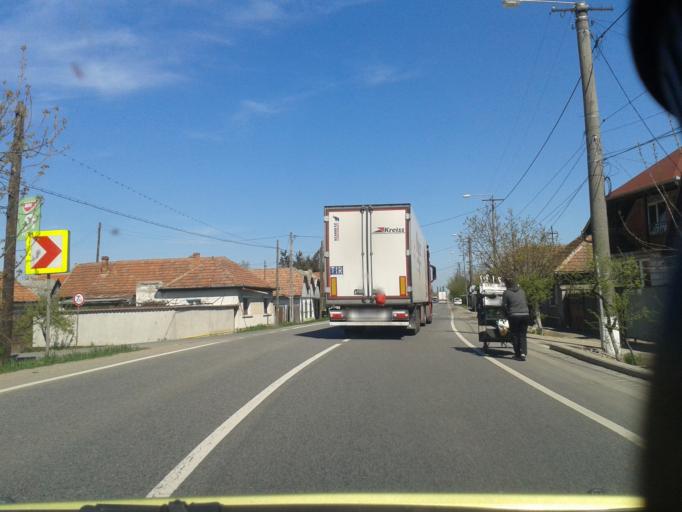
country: RO
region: Bihor
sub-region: Municipiul Salonta
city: Salonta
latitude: 46.8100
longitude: 21.6603
